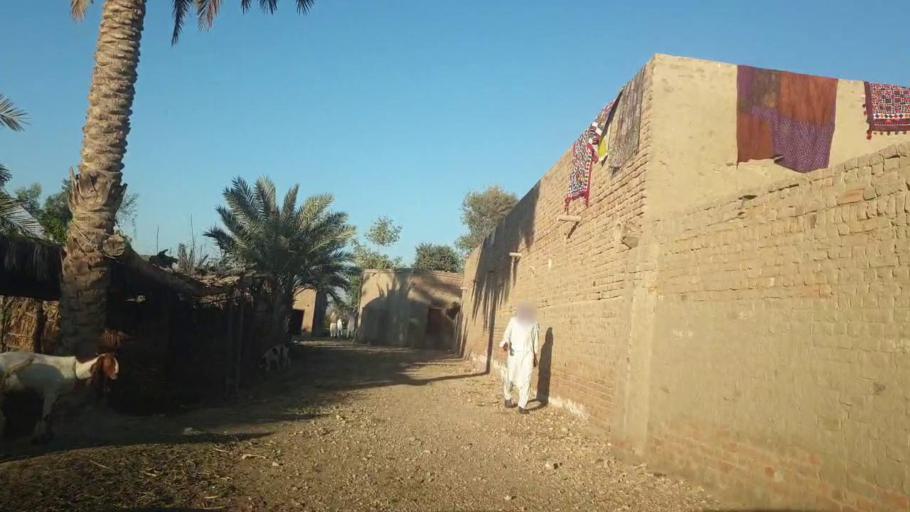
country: PK
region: Sindh
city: Ghotki
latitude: 28.0061
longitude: 69.2713
